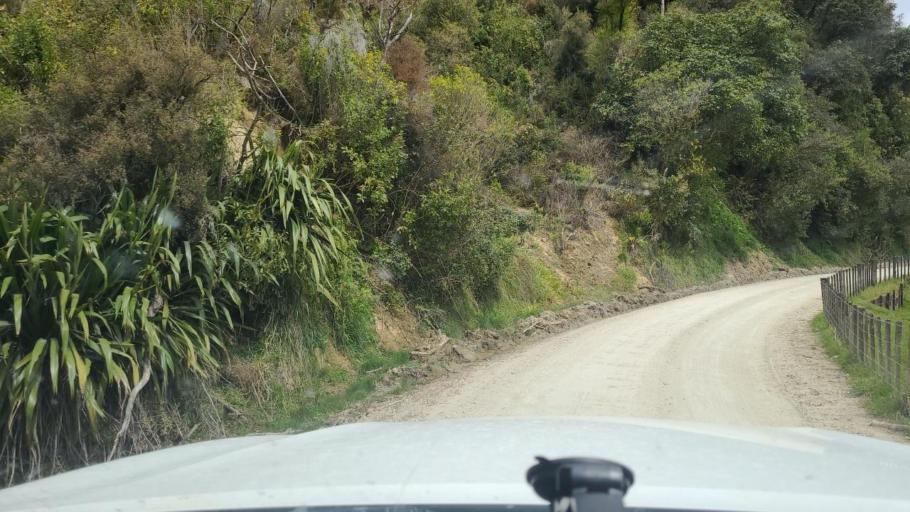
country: NZ
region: Gisborne
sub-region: Gisborne District
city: Gisborne
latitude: -38.8296
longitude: 177.7218
